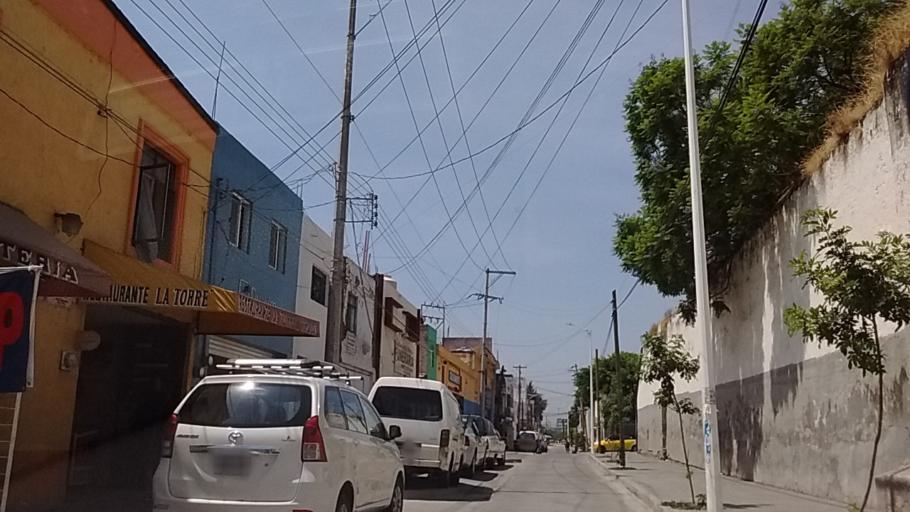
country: MX
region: Jalisco
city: Guadalajara
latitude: 20.6888
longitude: -103.3429
